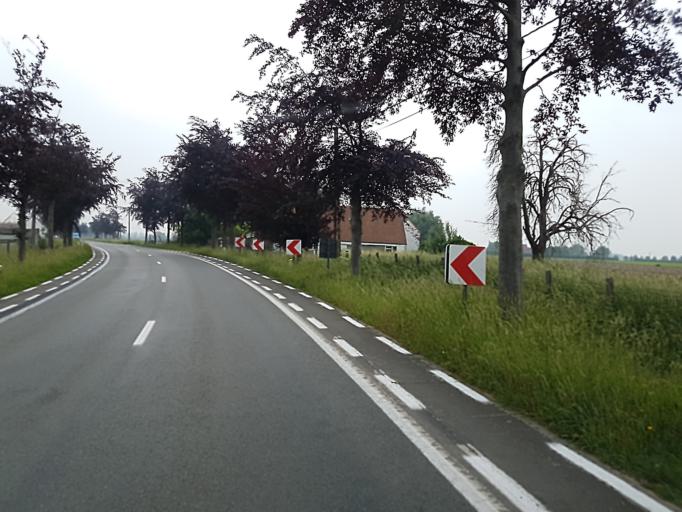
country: BE
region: Flanders
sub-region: Provincie West-Vlaanderen
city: Dentergem
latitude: 50.9543
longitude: 3.3730
